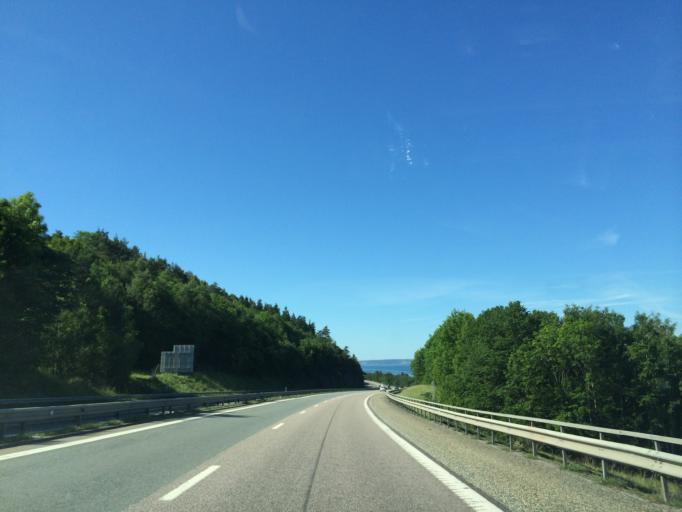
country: SE
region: Joenkoeping
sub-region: Jonkopings Kommun
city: Kaxholmen
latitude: 57.9151
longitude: 14.3095
